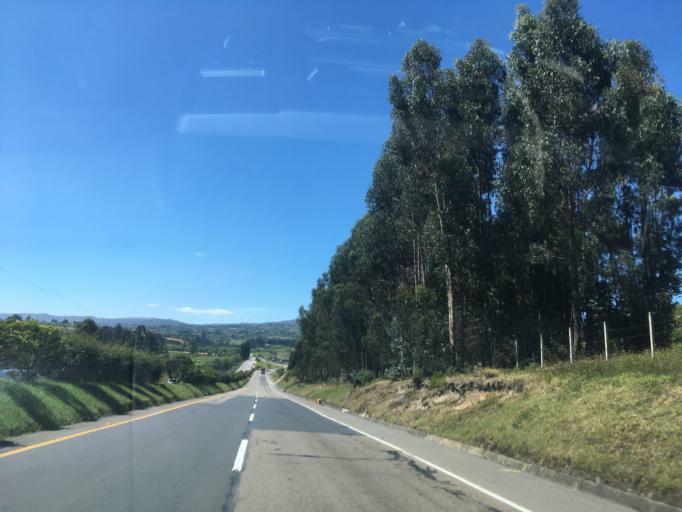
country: CO
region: Boyaca
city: Tuta
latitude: 5.7136
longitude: -73.2336
